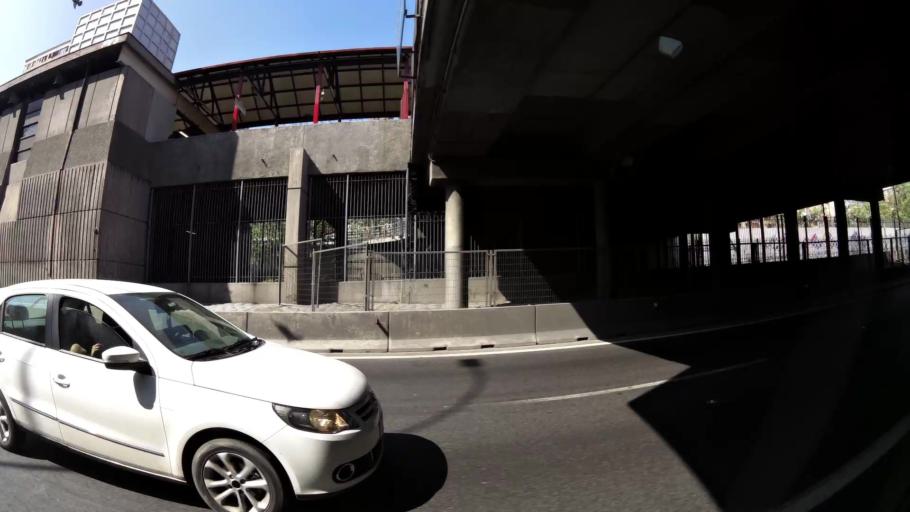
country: CL
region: Santiago Metropolitan
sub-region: Provincia de Santiago
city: Santiago
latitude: -33.4394
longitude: -70.6599
